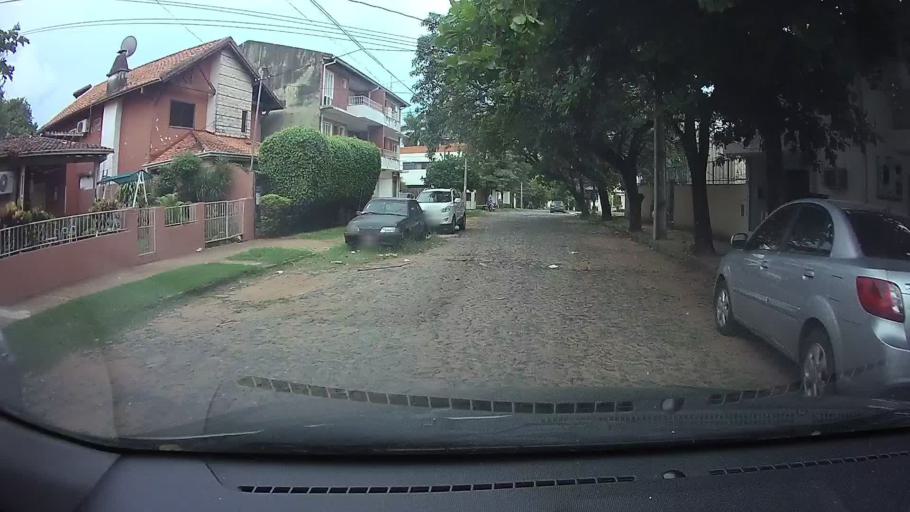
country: PY
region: Asuncion
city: Asuncion
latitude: -25.2787
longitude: -57.5721
